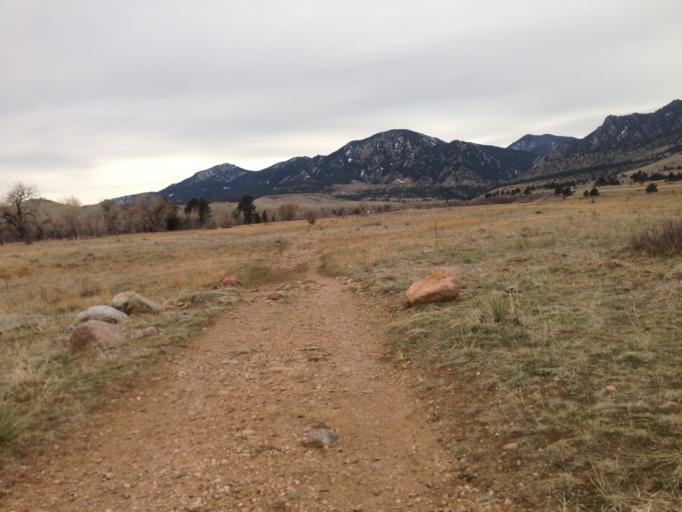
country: US
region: Colorado
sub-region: Boulder County
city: Boulder
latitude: 39.9515
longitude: -105.2444
